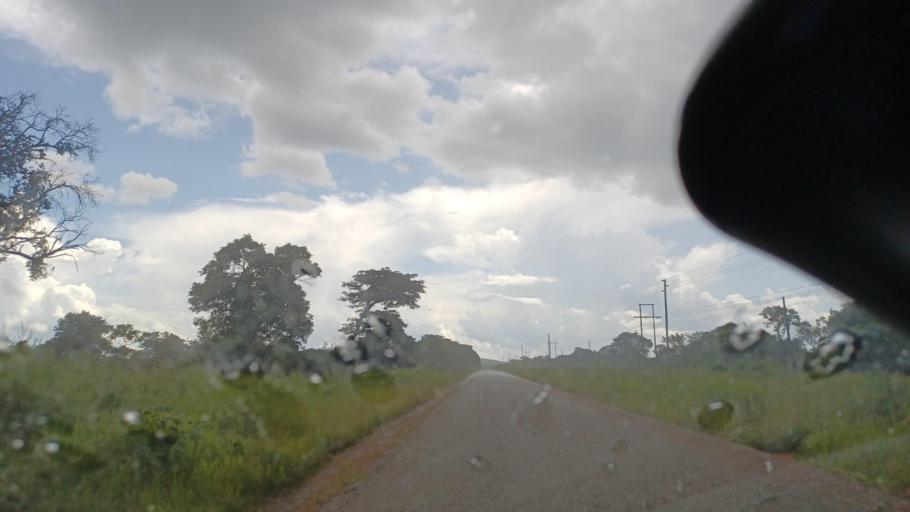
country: ZM
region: North-Western
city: Kasempa
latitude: -13.1010
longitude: 25.8938
